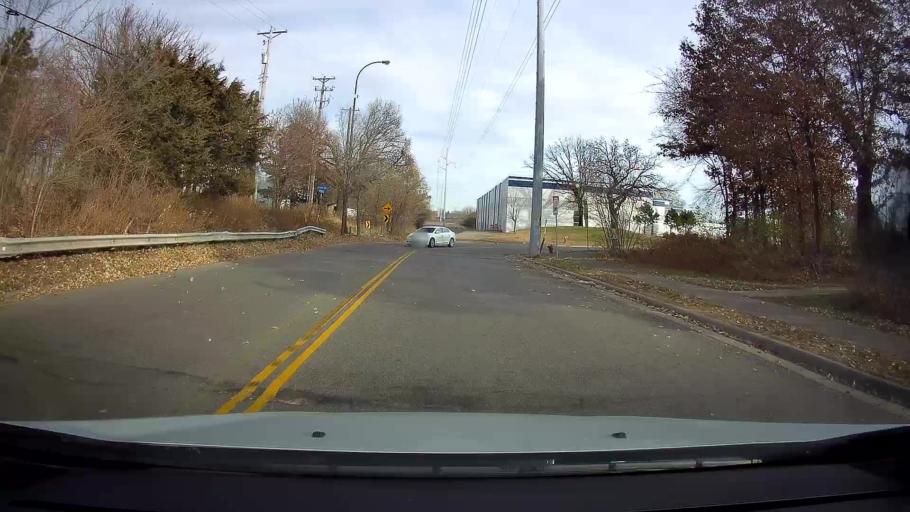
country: US
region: Minnesota
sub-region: Ramsey County
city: Lauderdale
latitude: 44.9843
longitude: -93.2176
